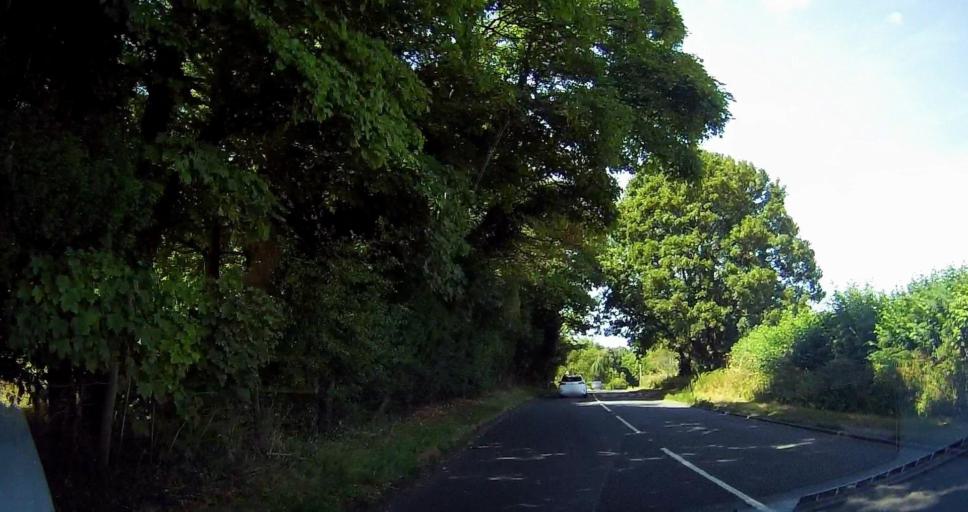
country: GB
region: England
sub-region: Shropshire
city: Albrighton
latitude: 52.6223
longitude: -2.2406
